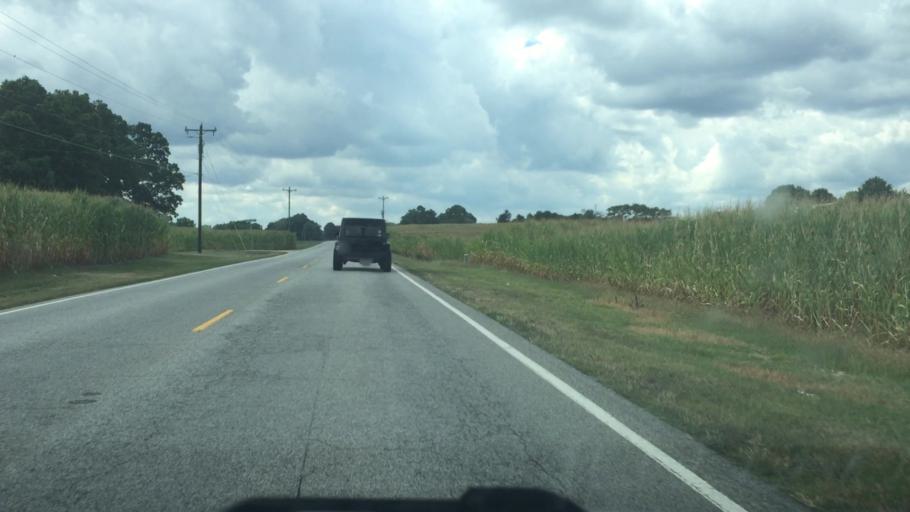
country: US
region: North Carolina
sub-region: Rowan County
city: Enochville
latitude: 35.5771
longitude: -80.6547
